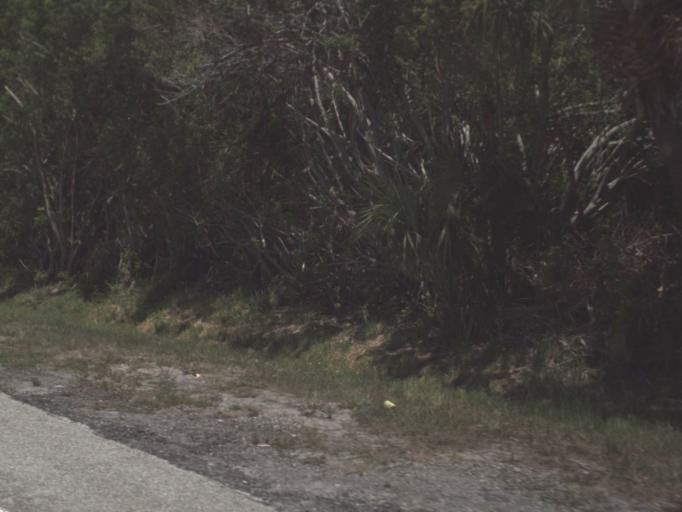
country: US
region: Florida
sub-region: Brevard County
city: Malabar
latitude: 27.9776
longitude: -80.5517
